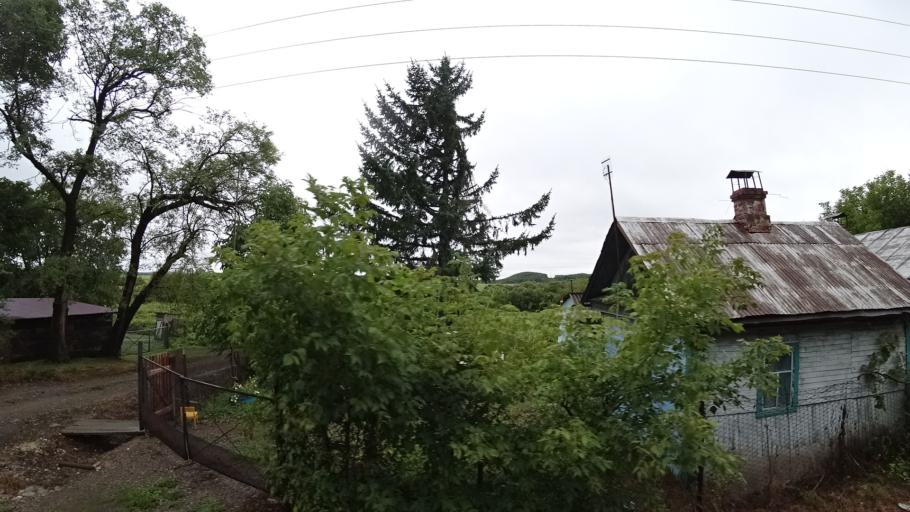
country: RU
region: Primorskiy
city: Monastyrishche
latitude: 44.2637
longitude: 132.4046
